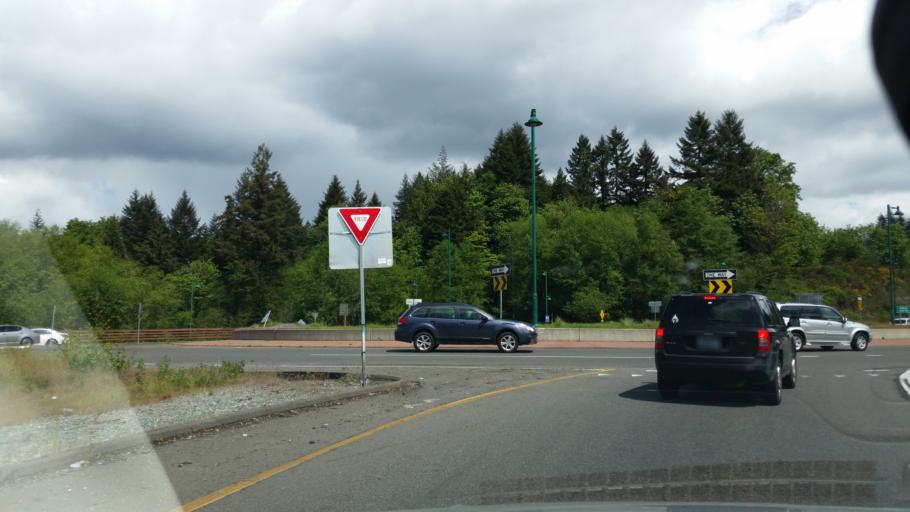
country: US
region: Washington
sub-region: Pierce County
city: Canterwood
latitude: 47.3581
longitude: -122.6133
